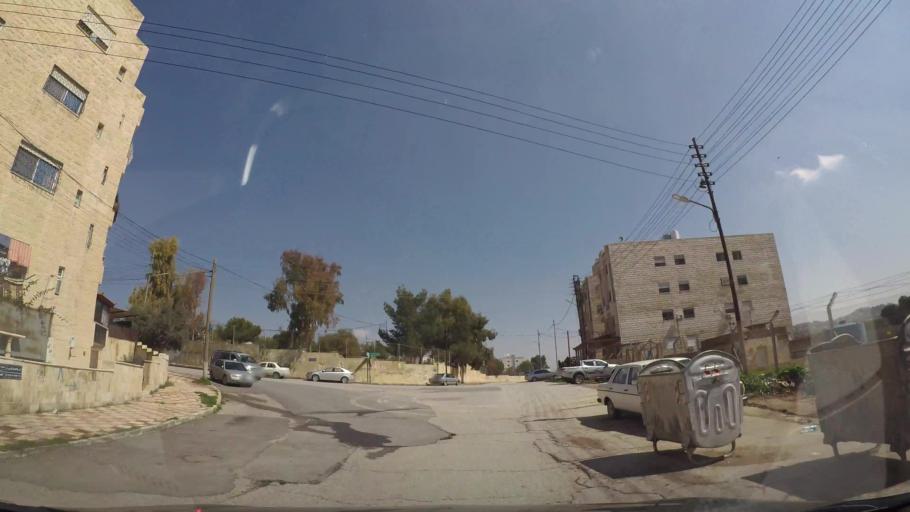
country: JO
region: Amman
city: Amman
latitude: 31.9776
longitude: 35.9968
